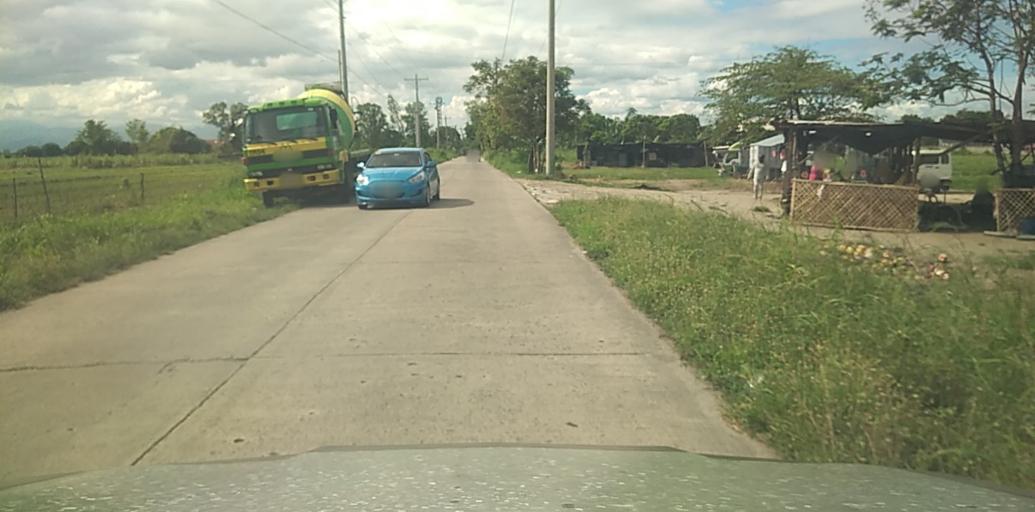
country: PH
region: Central Luzon
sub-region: Province of Pampanga
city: Pandacaqui
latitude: 15.1751
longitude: 120.6699
